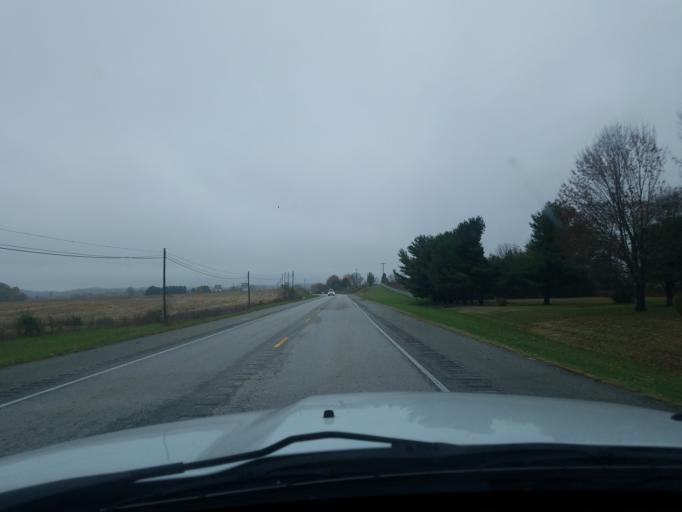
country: US
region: Kentucky
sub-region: Taylor County
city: Campbellsville
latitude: 37.3627
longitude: -85.3839
